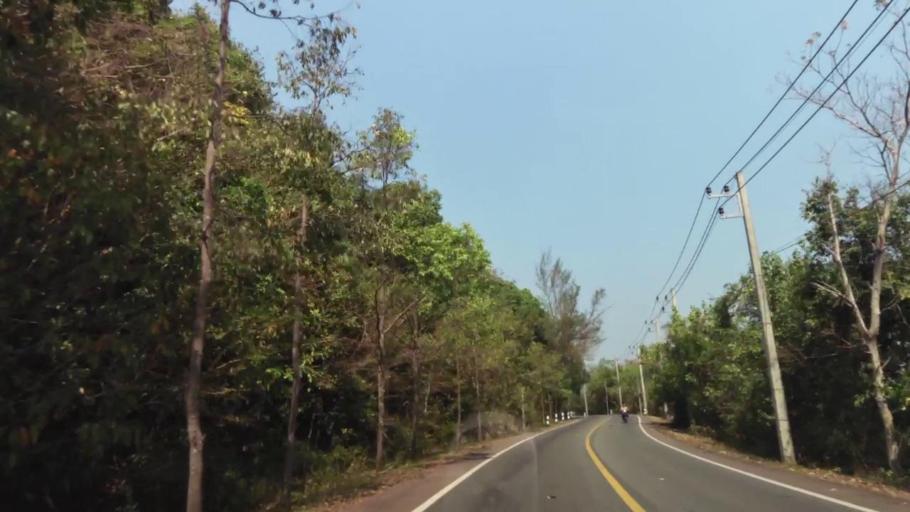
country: TH
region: Chanthaburi
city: Tha Mai
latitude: 12.5344
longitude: 101.9473
